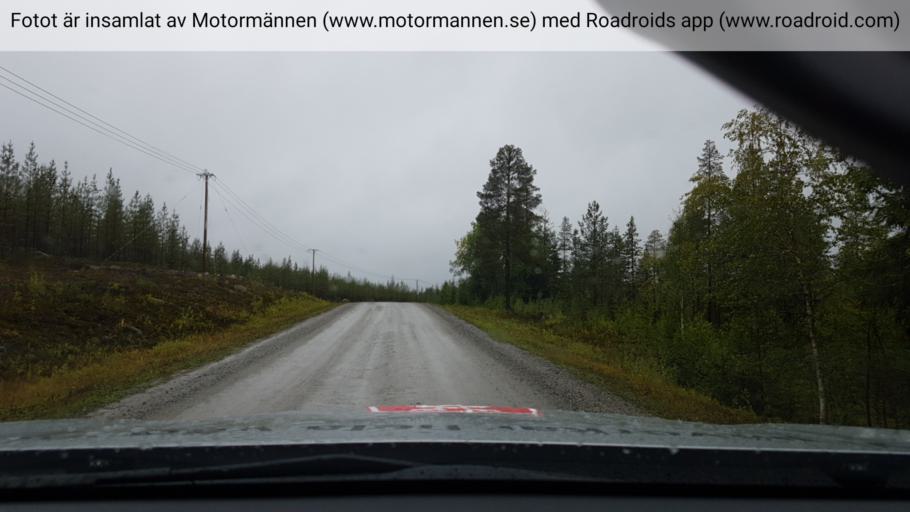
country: SE
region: Vaesterbotten
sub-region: Asele Kommun
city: Asele
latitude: 64.0697
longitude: 17.6813
